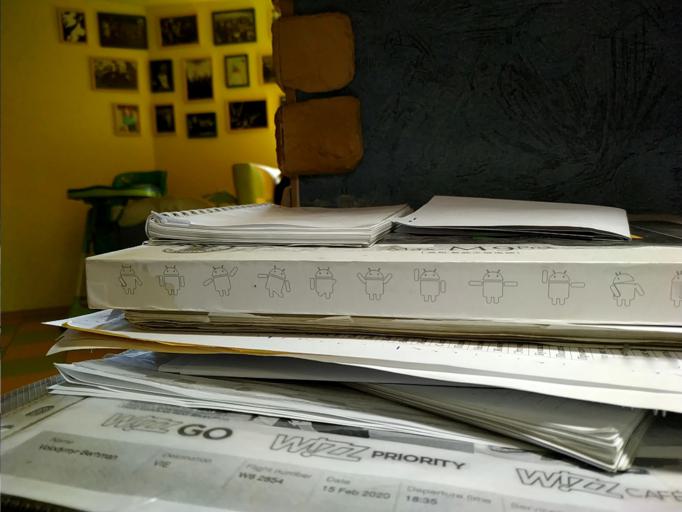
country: RU
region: Pskov
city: Plyussa
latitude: 58.5103
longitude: 29.5396
